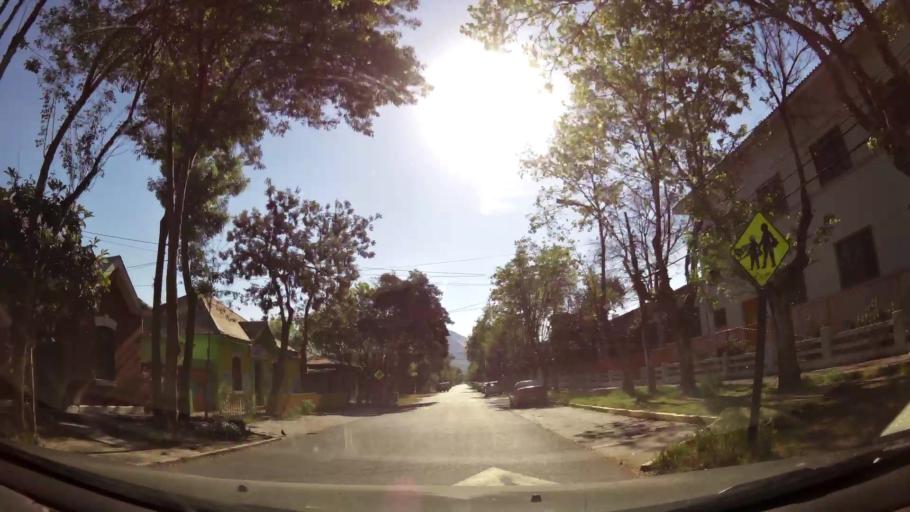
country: CL
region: Santiago Metropolitan
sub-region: Provincia de Maipo
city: San Bernardo
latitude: -33.6045
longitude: -70.6979
